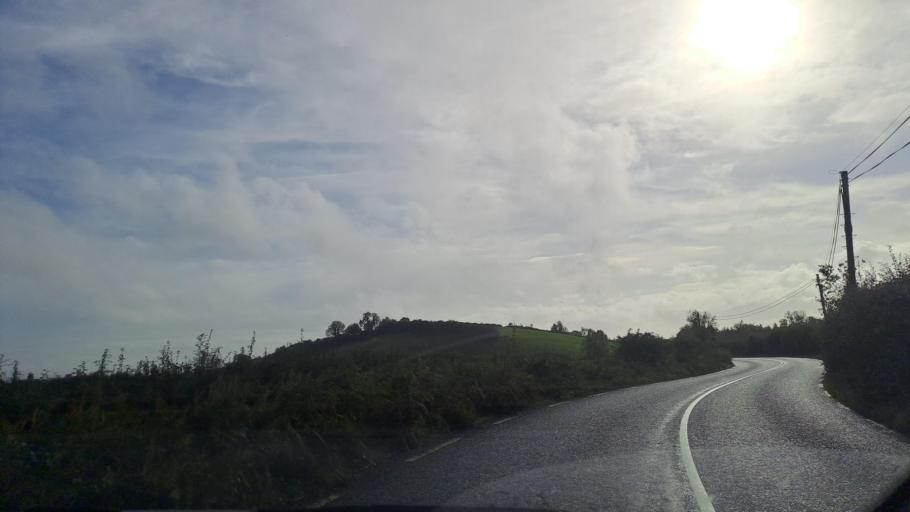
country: IE
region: Ulster
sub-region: County Monaghan
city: Carrickmacross
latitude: 53.9321
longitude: -6.7154
